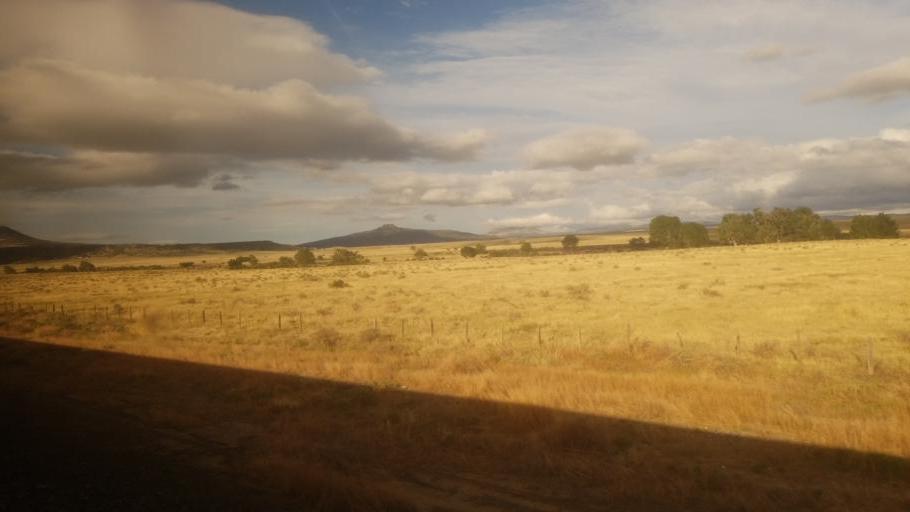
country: US
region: New Mexico
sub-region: Colfax County
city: Raton
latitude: 36.6314
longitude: -104.5033
